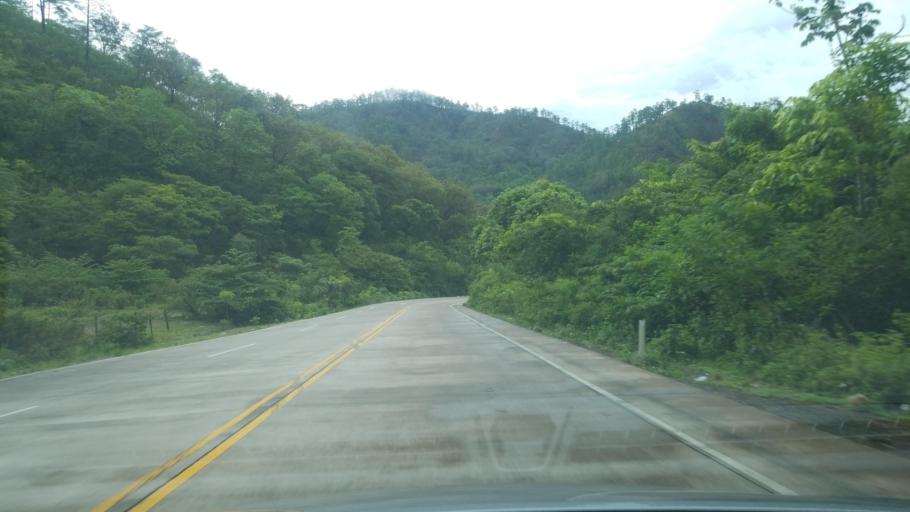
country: HN
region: Copan
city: Copan
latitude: 14.8543
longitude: -89.2177
